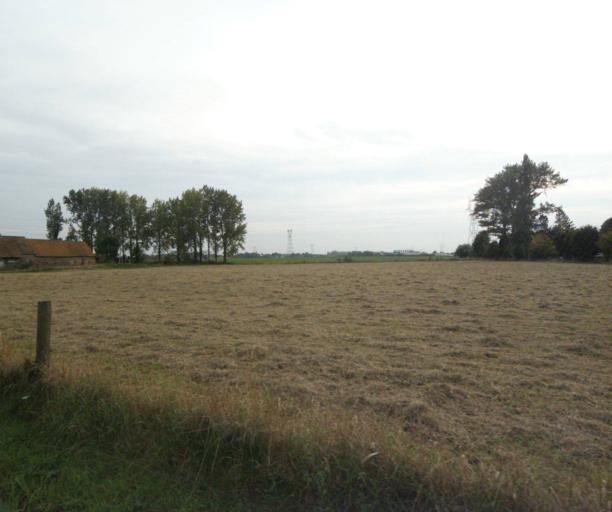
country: FR
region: Nord-Pas-de-Calais
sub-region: Departement du Nord
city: Seclin
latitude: 50.5305
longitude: 3.0326
